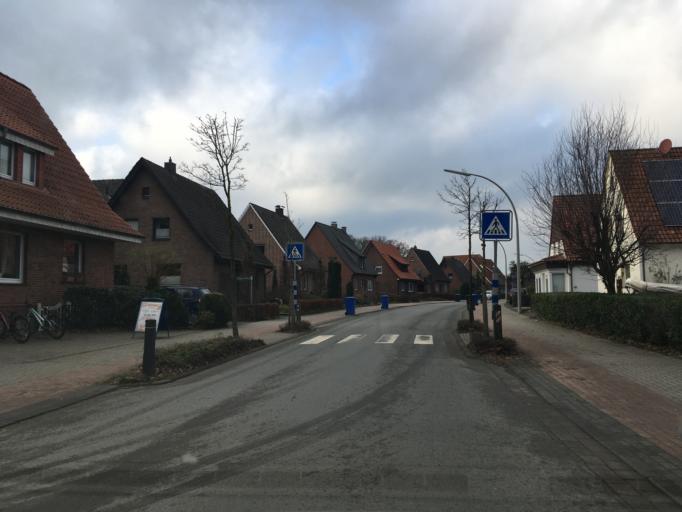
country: DE
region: North Rhine-Westphalia
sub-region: Regierungsbezirk Munster
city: Gescher
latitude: 51.9488
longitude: 7.0019
